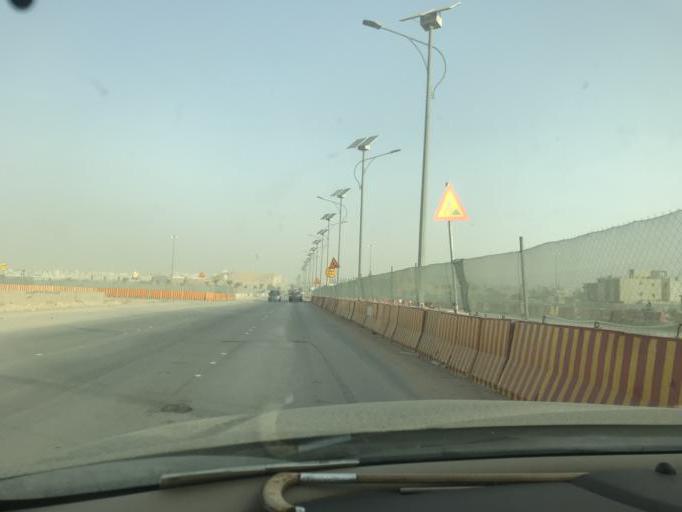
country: SA
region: Ar Riyad
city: Riyadh
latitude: 24.8447
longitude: 46.6647
